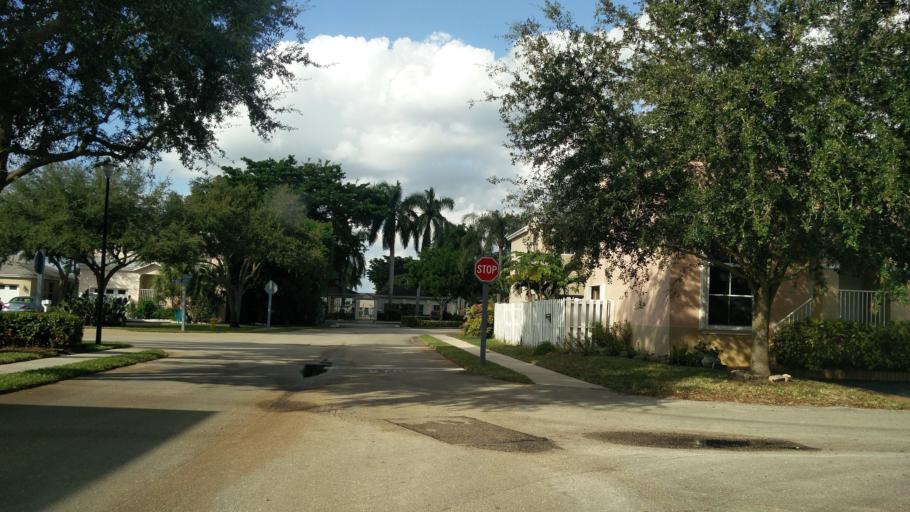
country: US
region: Florida
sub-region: Broward County
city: Davie
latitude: 26.0685
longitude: -80.2428
